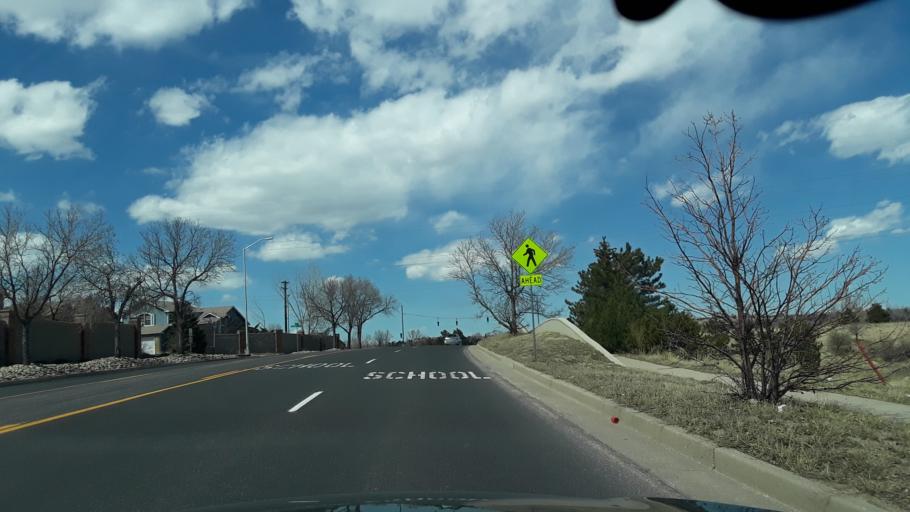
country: US
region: Colorado
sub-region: El Paso County
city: Black Forest
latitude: 38.9394
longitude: -104.7629
